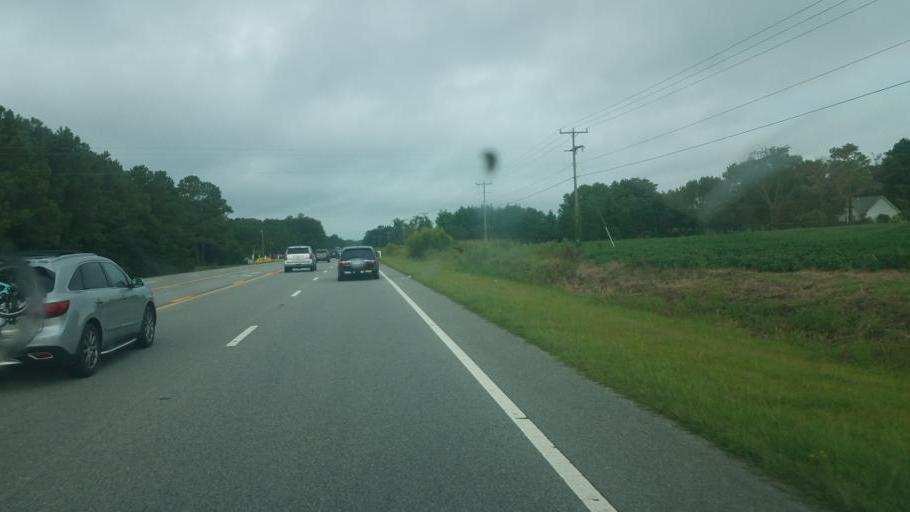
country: US
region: North Carolina
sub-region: Currituck County
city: Currituck
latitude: 36.4555
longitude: -76.0365
